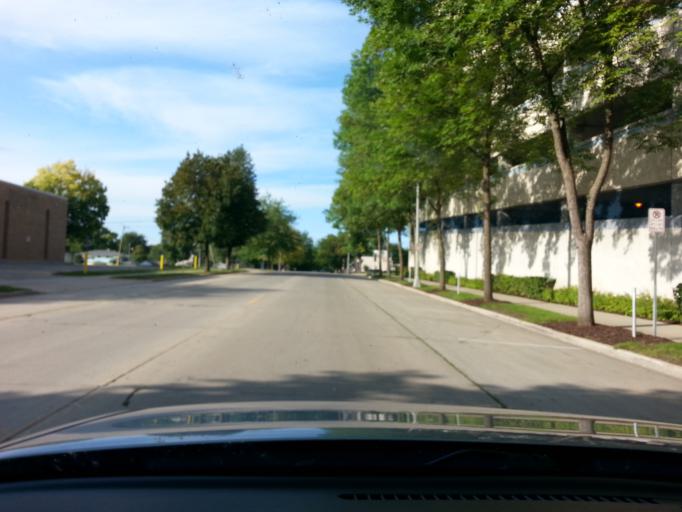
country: US
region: Minnesota
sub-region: Olmsted County
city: Rochester
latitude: 44.0237
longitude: -92.4710
